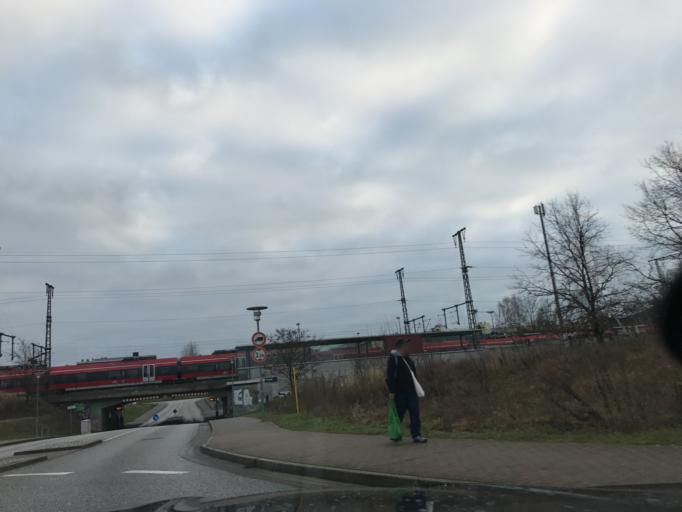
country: DE
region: Brandenburg
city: Werder
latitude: 52.4106
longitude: 12.9708
